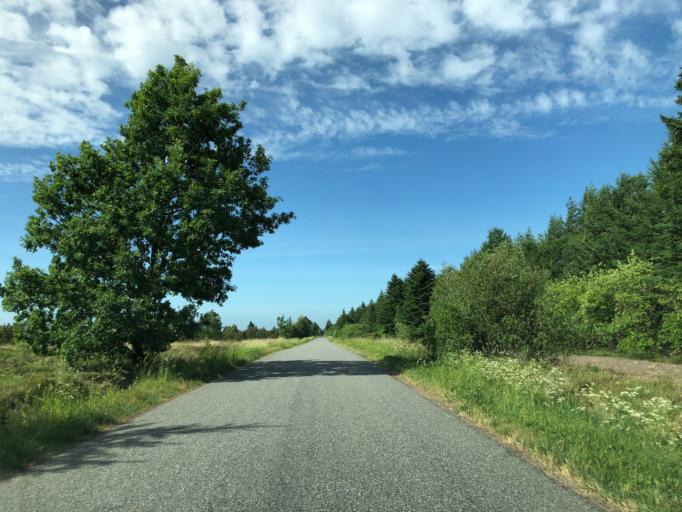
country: DK
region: Central Jutland
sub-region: Herning Kommune
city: Kibaek
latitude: 56.0697
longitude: 8.9154
